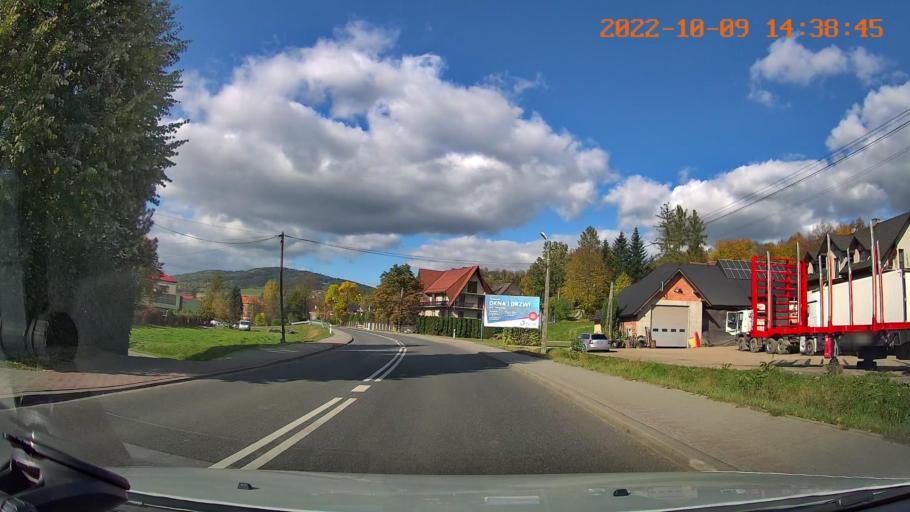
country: PL
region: Lesser Poland Voivodeship
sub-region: Powiat limanowski
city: Mszana Dolna
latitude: 49.6970
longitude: 20.0419
